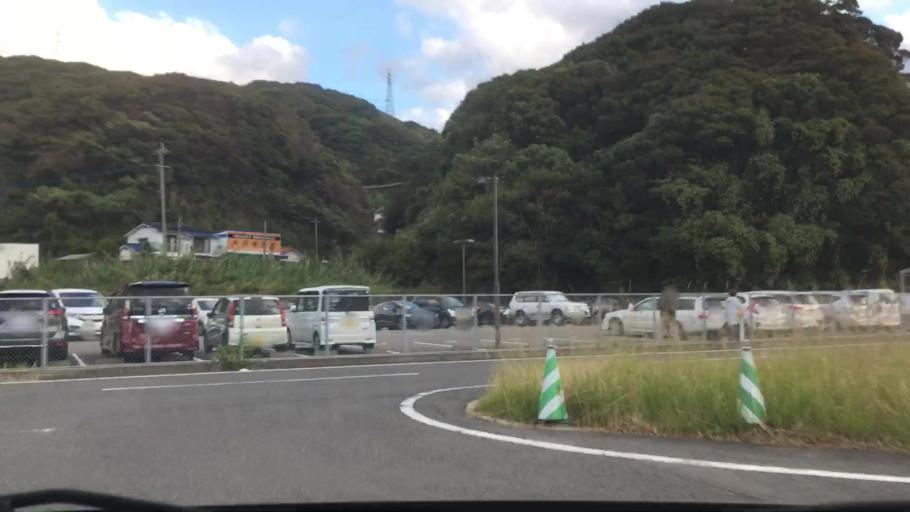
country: JP
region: Nagasaki
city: Sasebo
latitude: 32.9423
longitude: 129.6391
